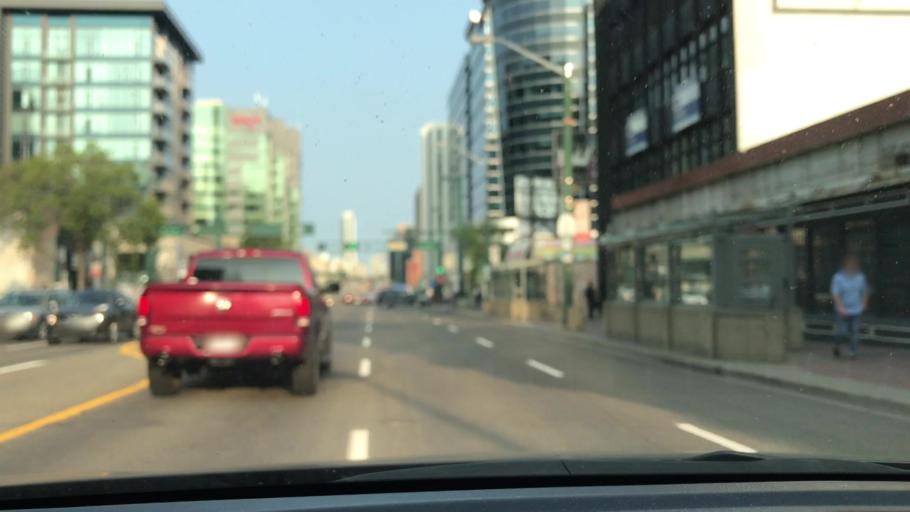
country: CA
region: Alberta
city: Edmonton
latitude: 53.5409
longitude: -113.5054
